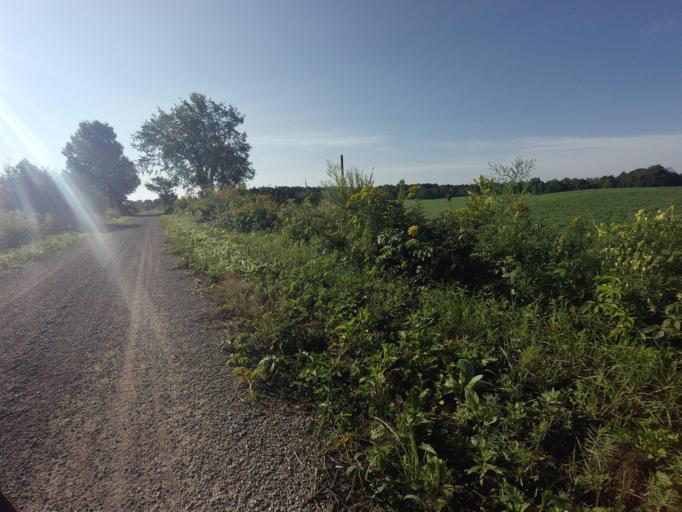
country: CA
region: Ontario
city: Goderich
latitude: 43.7542
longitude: -81.5102
